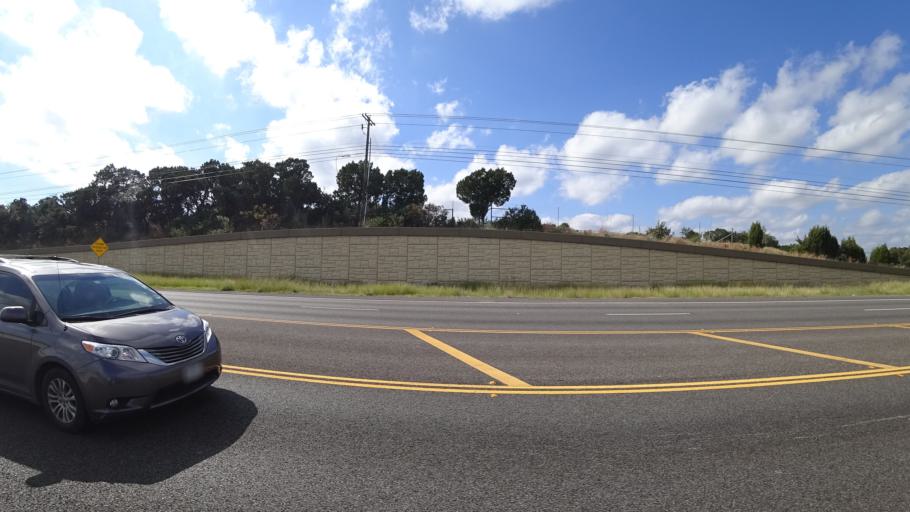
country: US
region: Texas
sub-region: Travis County
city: Bee Cave
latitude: 30.2793
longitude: -97.9162
